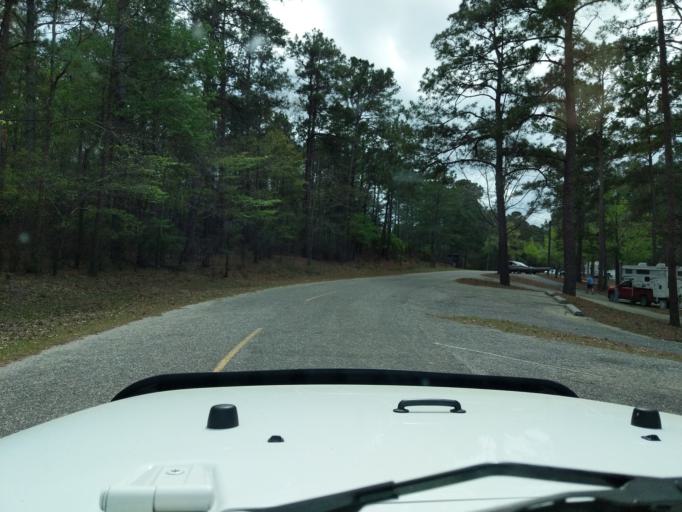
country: US
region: Georgia
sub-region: Clay County
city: Fort Gaines
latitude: 31.6754
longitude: -85.0644
